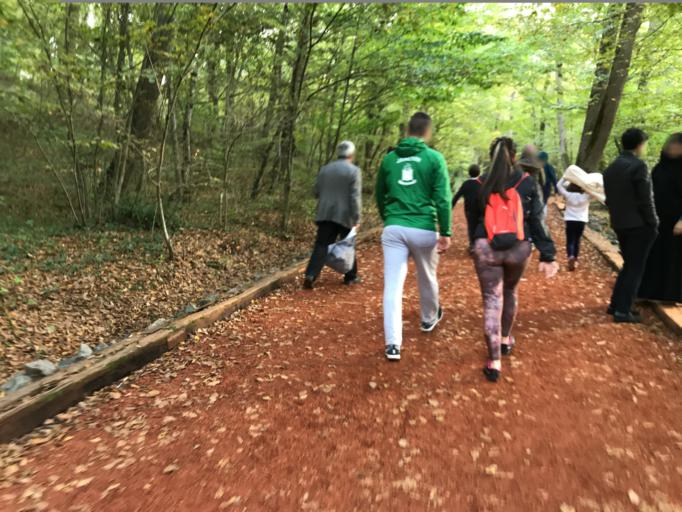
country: TR
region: Istanbul
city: Kemerburgaz
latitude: 41.1767
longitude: 28.9594
